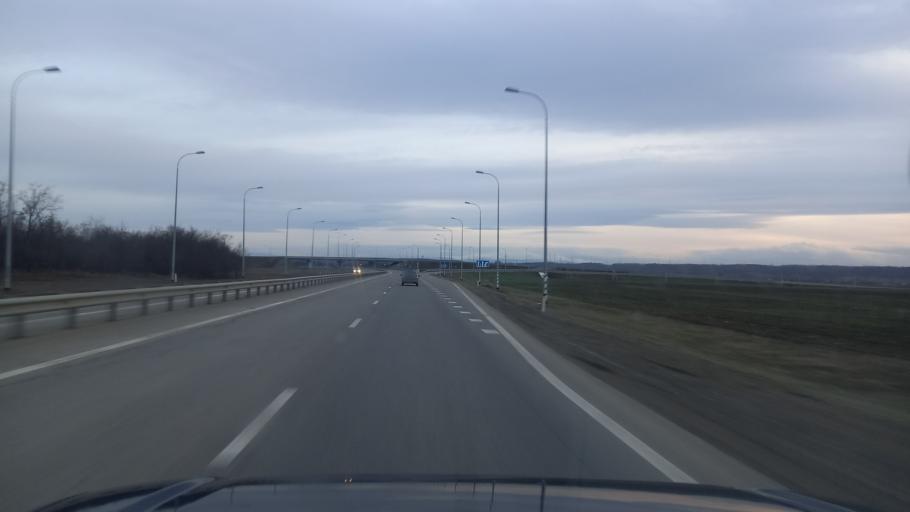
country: RU
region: Adygeya
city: Khanskaya
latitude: 44.6641
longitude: 39.9934
